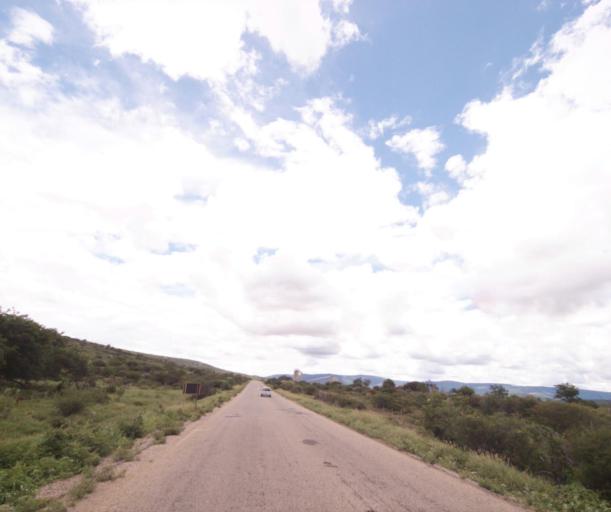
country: BR
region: Bahia
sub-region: Brumado
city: Brumado
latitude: -14.1974
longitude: -41.5878
